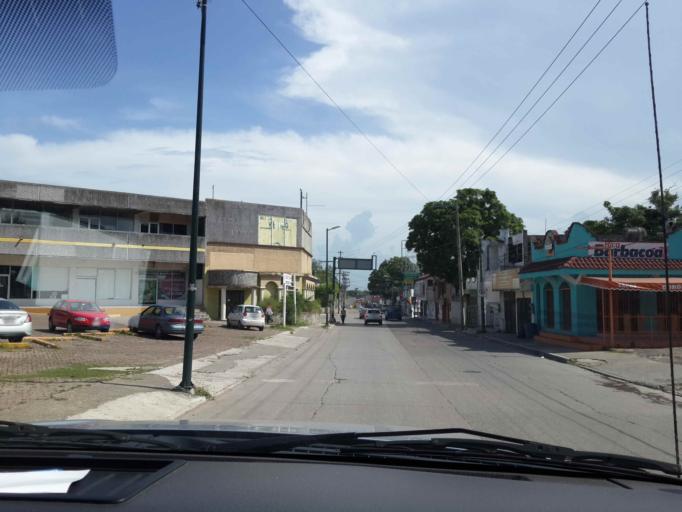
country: MX
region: Tamaulipas
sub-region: Tampico
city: Tampico
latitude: 22.2503
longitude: -97.8671
